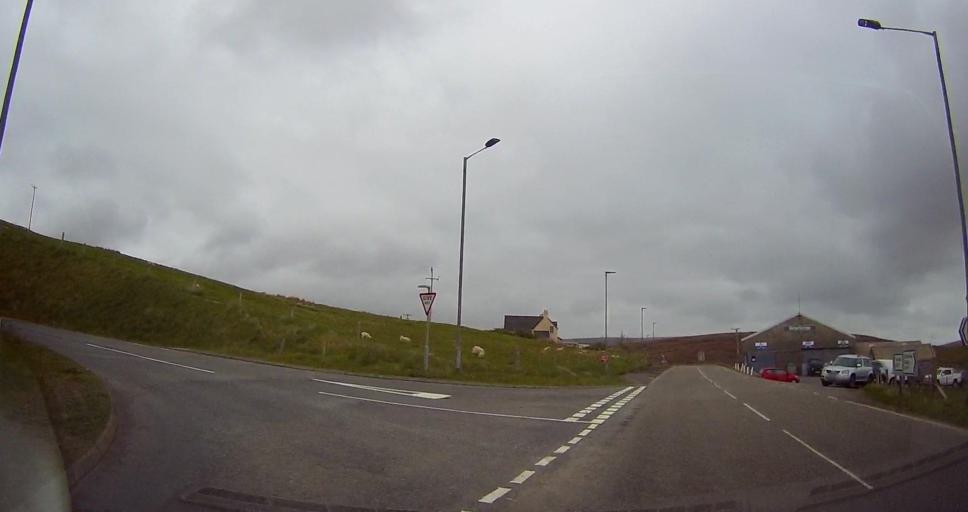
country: GB
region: Scotland
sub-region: Shetland Islands
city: Lerwick
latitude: 60.2541
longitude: -1.4053
